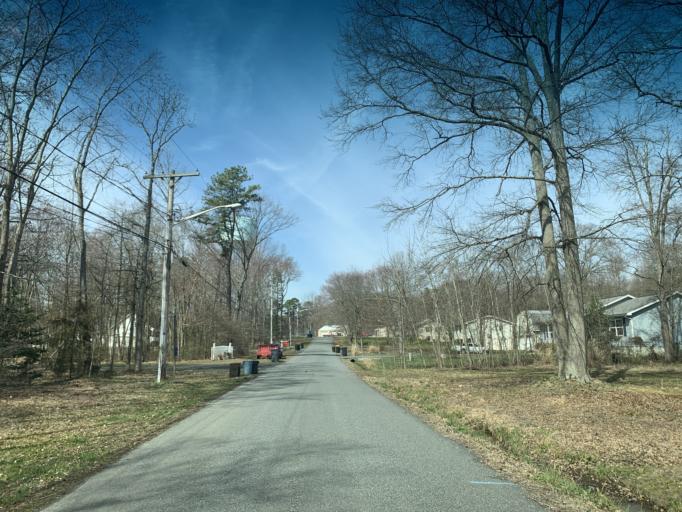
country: US
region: Maryland
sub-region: Cecil County
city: Charlestown
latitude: 39.5766
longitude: -75.9794
